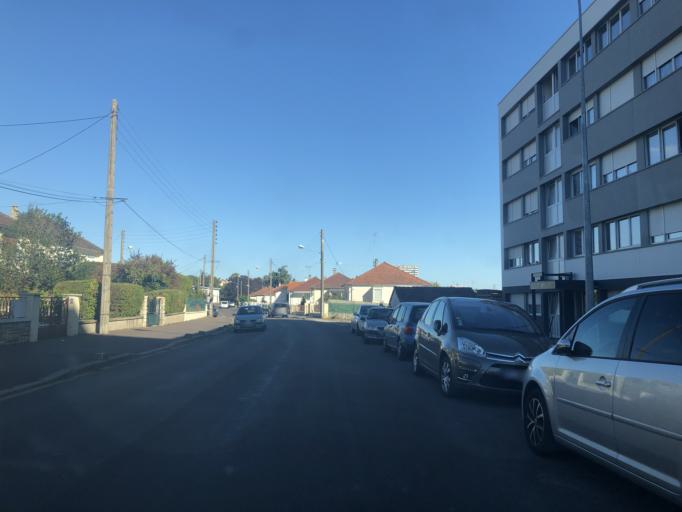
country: FR
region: Bourgogne
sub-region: Departement de l'Yonne
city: Joigny
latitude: 47.9806
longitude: 3.4158
